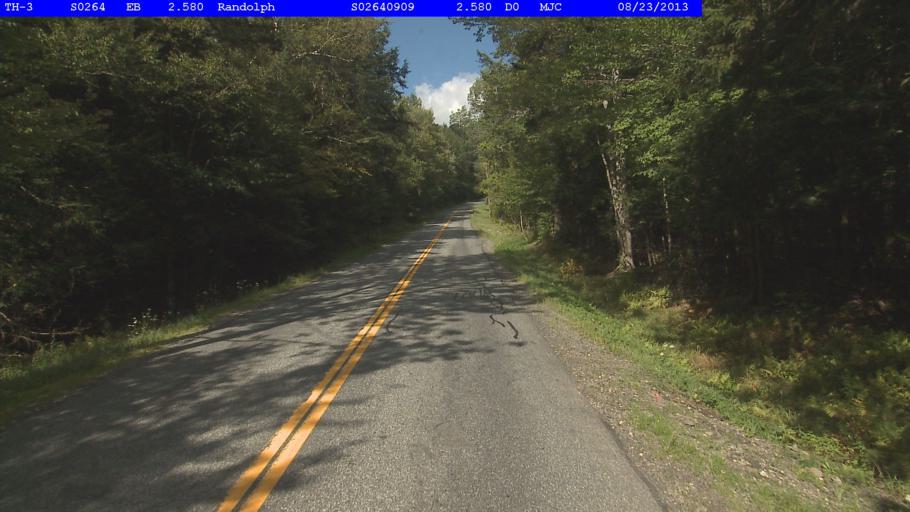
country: US
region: Vermont
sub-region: Orange County
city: Chelsea
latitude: 43.9625
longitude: -72.5270
